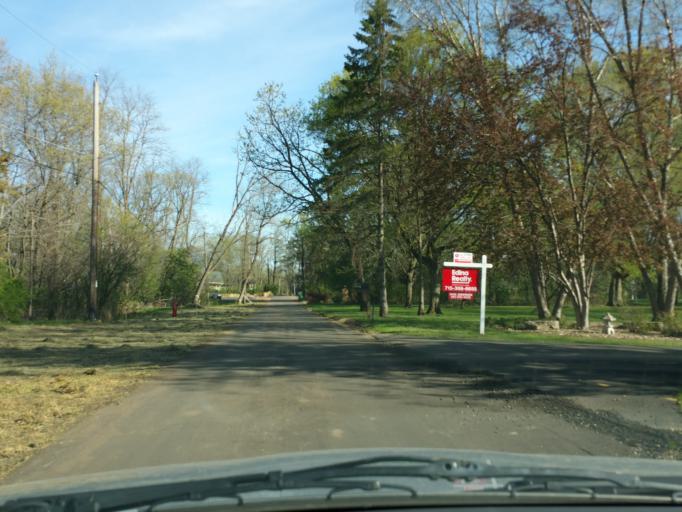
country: US
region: Wisconsin
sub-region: Saint Croix County
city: Hudson
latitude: 44.9655
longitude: -92.7509
